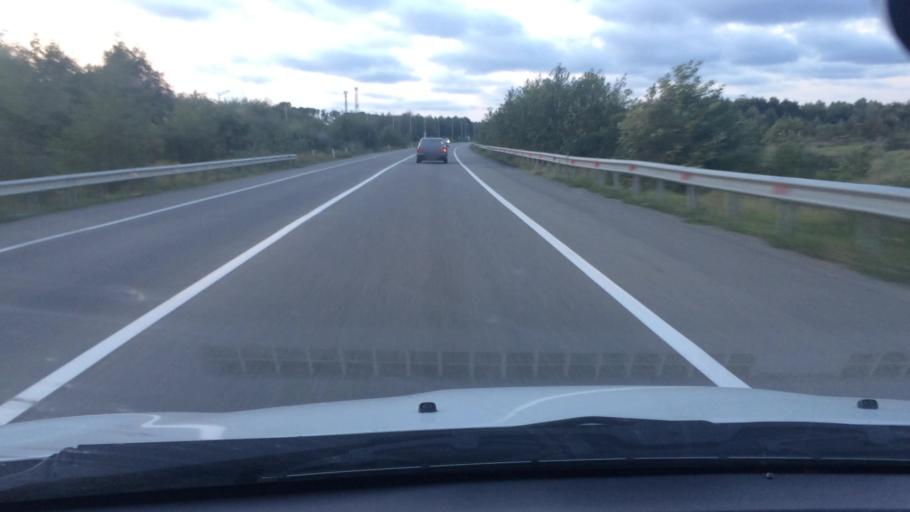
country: GE
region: Guria
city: Urek'i
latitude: 41.9200
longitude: 41.7745
